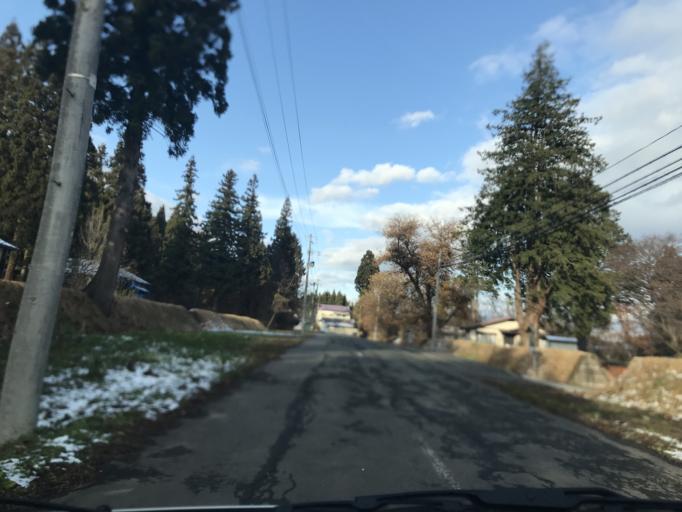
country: JP
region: Iwate
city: Kitakami
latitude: 39.2332
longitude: 141.0504
